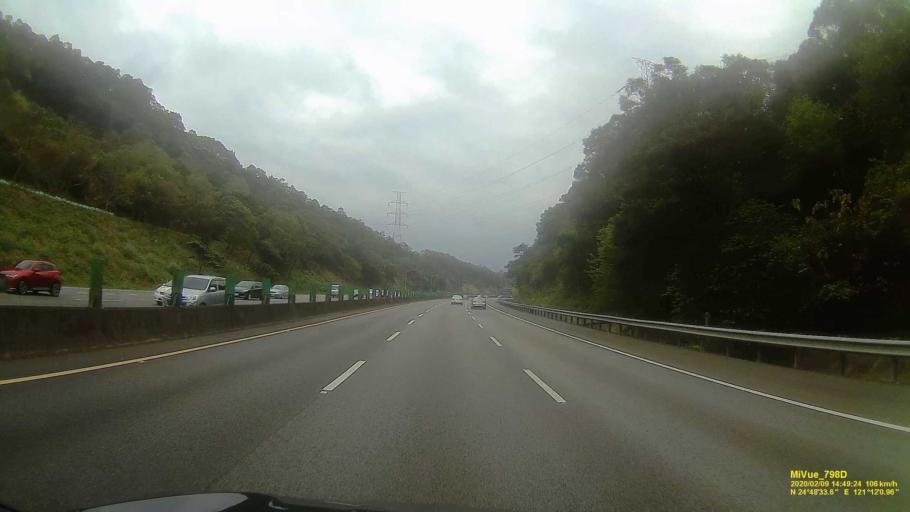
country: TW
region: Taiwan
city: Daxi
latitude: 24.8094
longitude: 121.2000
